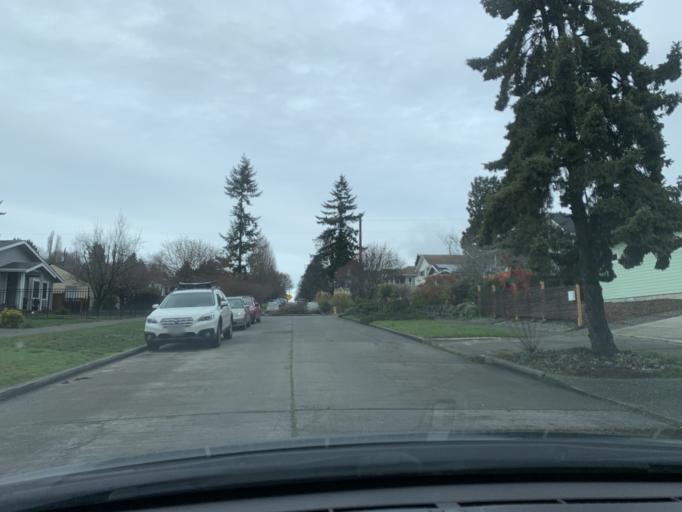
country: US
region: Washington
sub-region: King County
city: White Center
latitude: 47.5625
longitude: -122.3921
